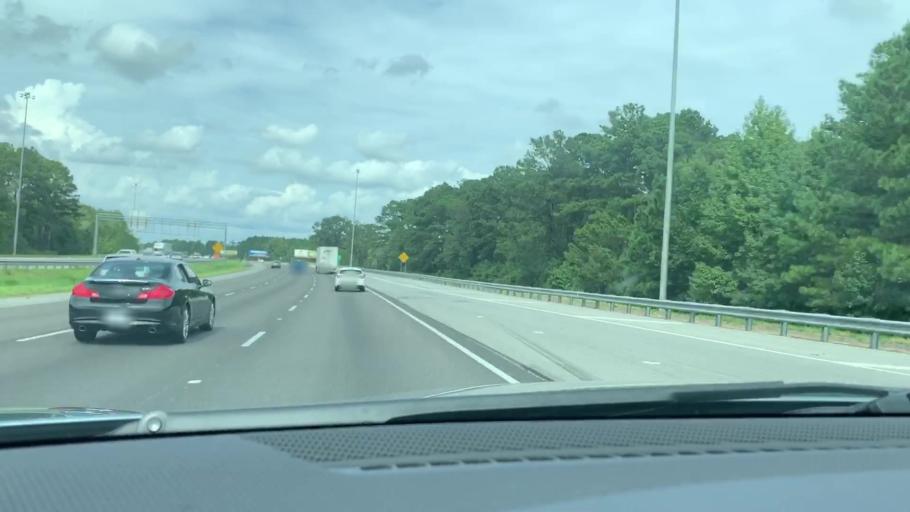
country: US
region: Georgia
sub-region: Liberty County
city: Midway
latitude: 31.6566
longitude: -81.3934
